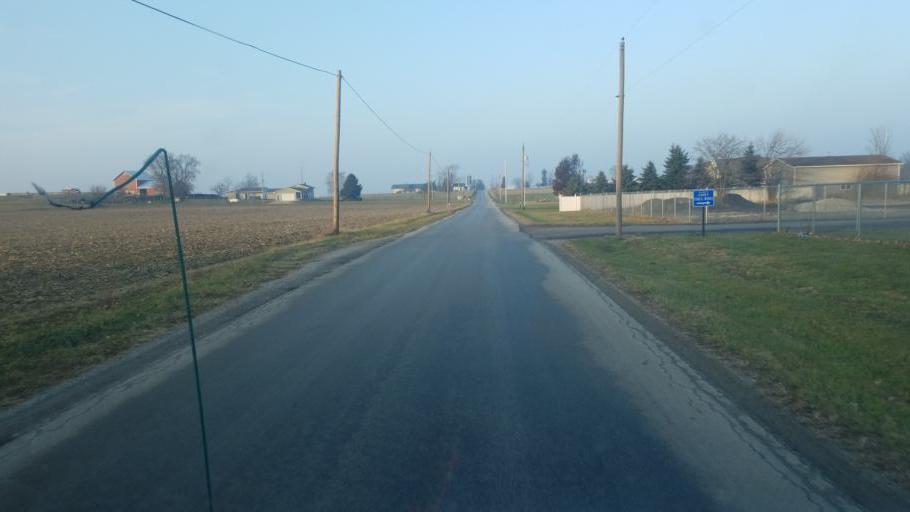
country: US
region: Ohio
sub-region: Wyandot County
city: Carey
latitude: 40.9590
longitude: -83.4060
